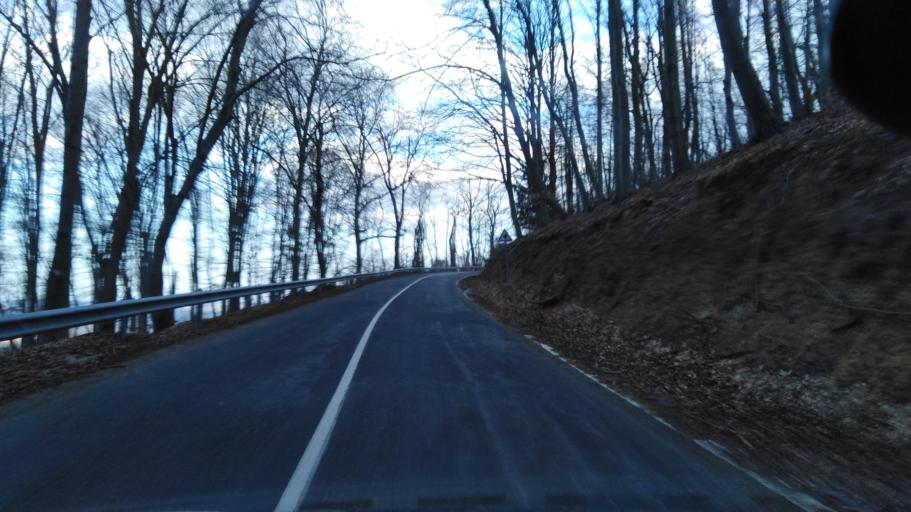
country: HU
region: Nograd
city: Matraterenye
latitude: 48.1303
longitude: 19.9405
